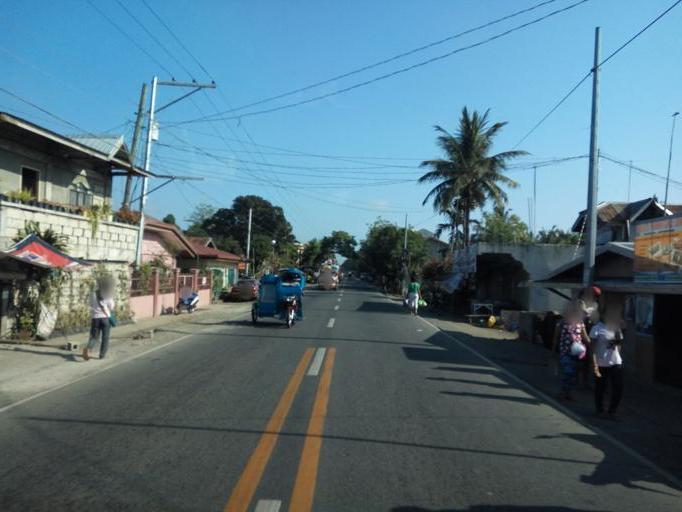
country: PH
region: Cagayan Valley
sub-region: Province of Cagayan
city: Amulung
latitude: 17.8394
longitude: 121.7230
